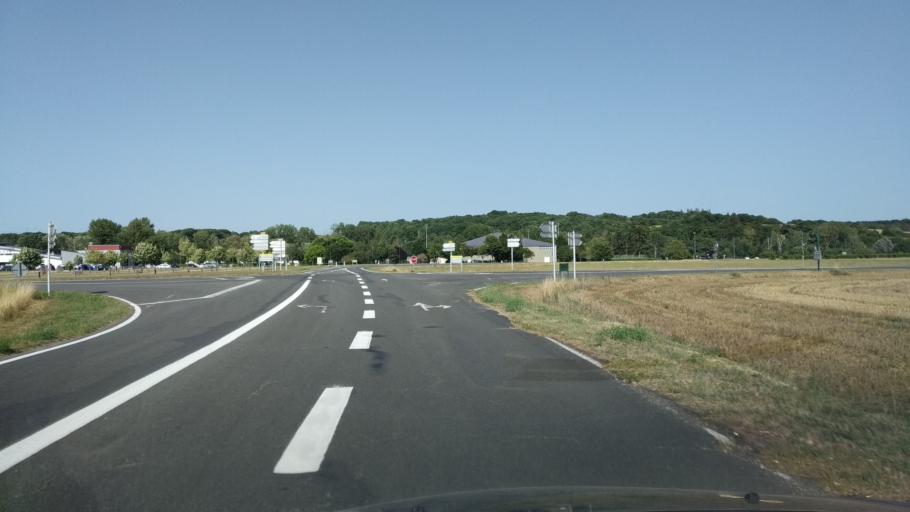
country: FR
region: Poitou-Charentes
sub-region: Departement de la Vienne
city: Lussac-les-Chateaux
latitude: 46.4477
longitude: 0.6631
